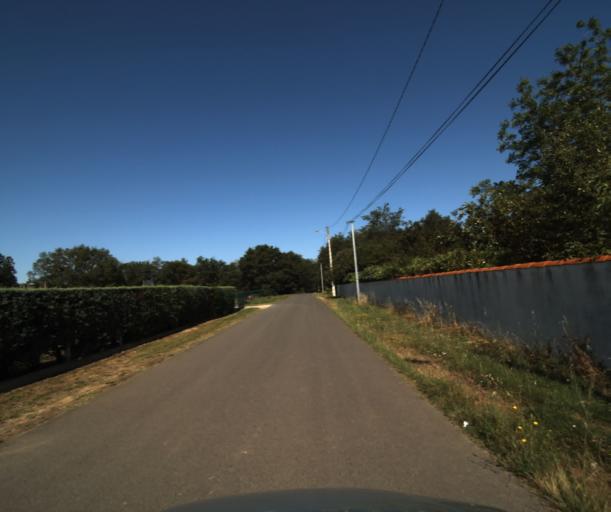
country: FR
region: Midi-Pyrenees
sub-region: Departement de la Haute-Garonne
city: Eaunes
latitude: 43.4357
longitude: 1.3585
